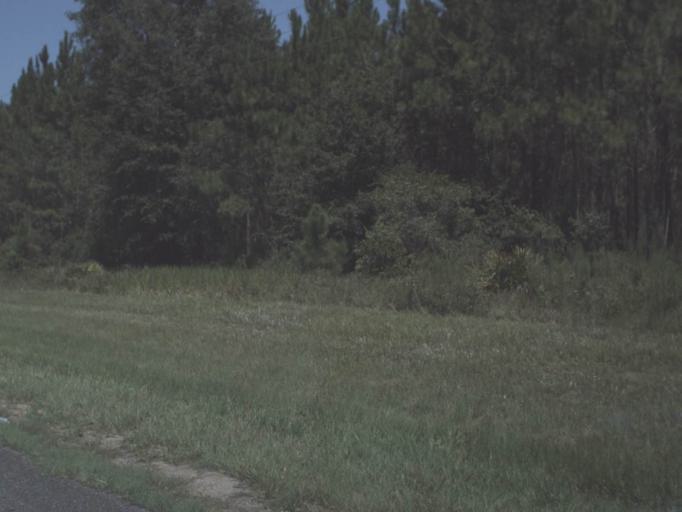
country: US
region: Florida
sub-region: Taylor County
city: Perry
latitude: 30.0996
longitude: -83.4603
